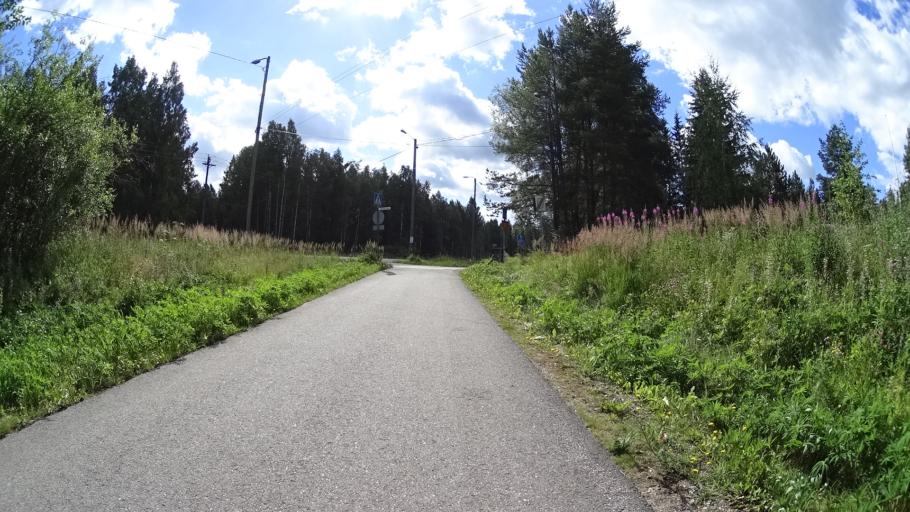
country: FI
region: Uusimaa
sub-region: Helsinki
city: Tuusula
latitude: 60.4246
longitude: 25.0531
